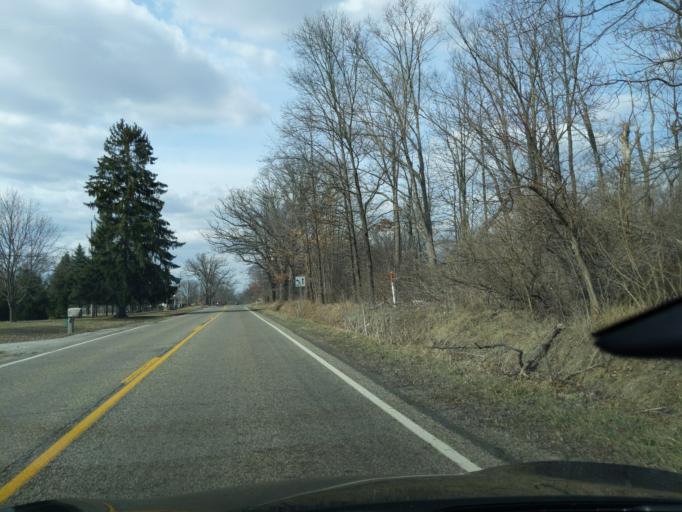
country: US
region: Michigan
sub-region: Jackson County
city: Jackson
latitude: 42.3258
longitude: -84.4136
